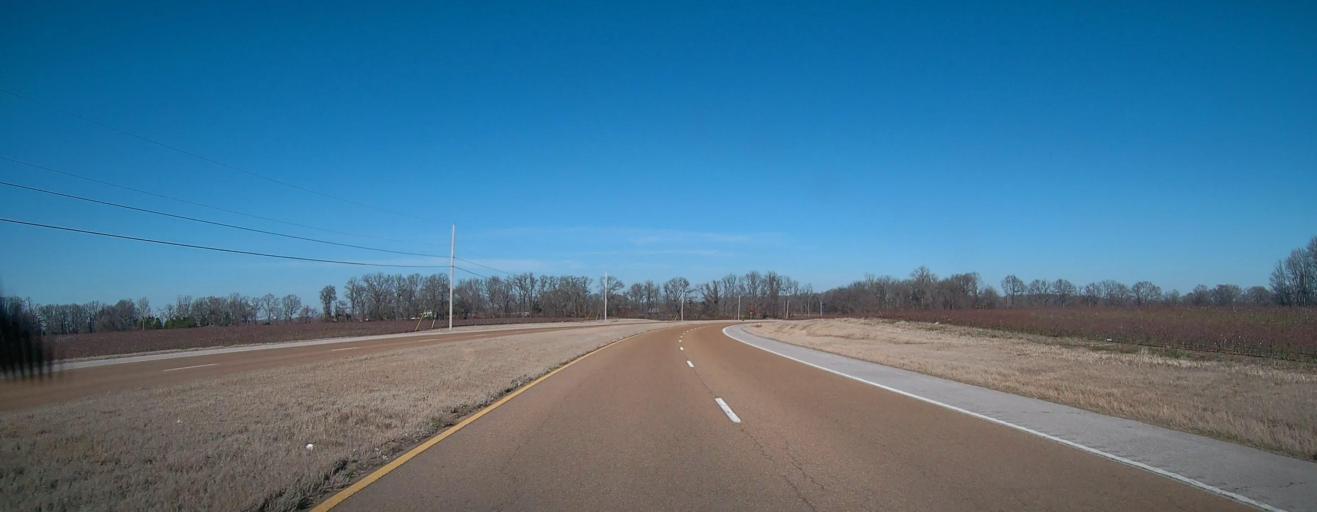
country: US
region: Tennessee
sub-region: Shelby County
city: Millington
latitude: 35.3080
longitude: -89.8816
